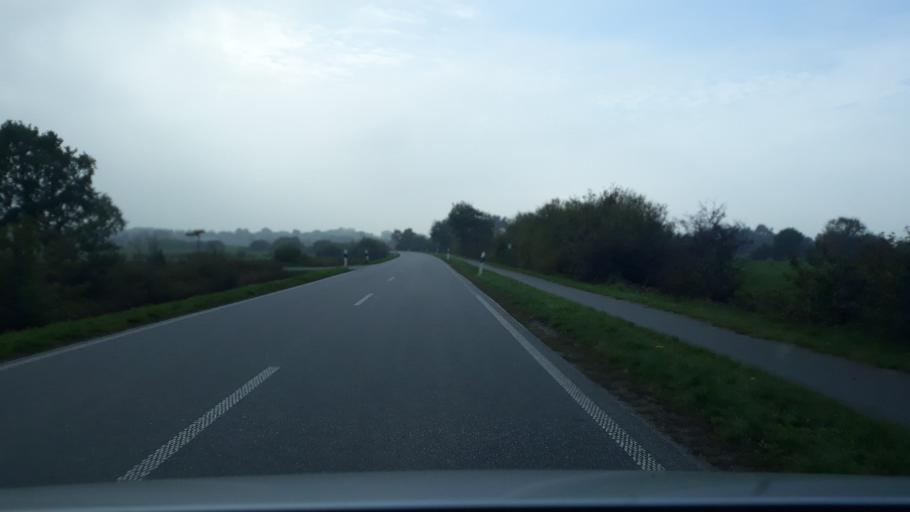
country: DE
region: Schleswig-Holstein
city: Klein Rheide
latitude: 54.4597
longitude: 9.4814
